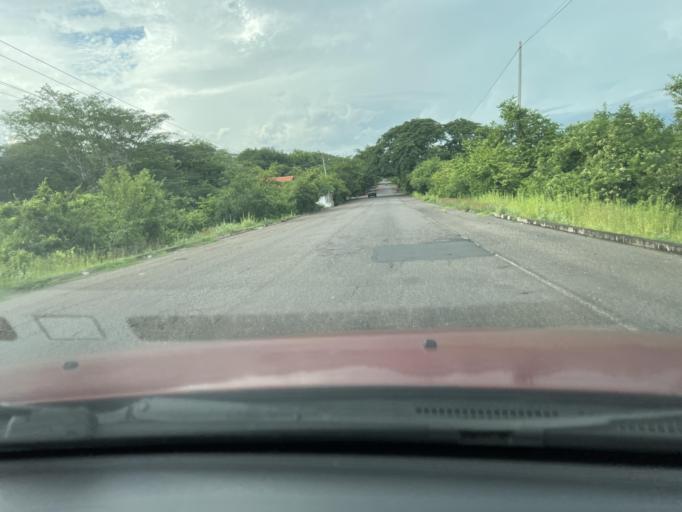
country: SV
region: La Union
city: San Alejo
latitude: 13.4047
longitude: -87.8933
